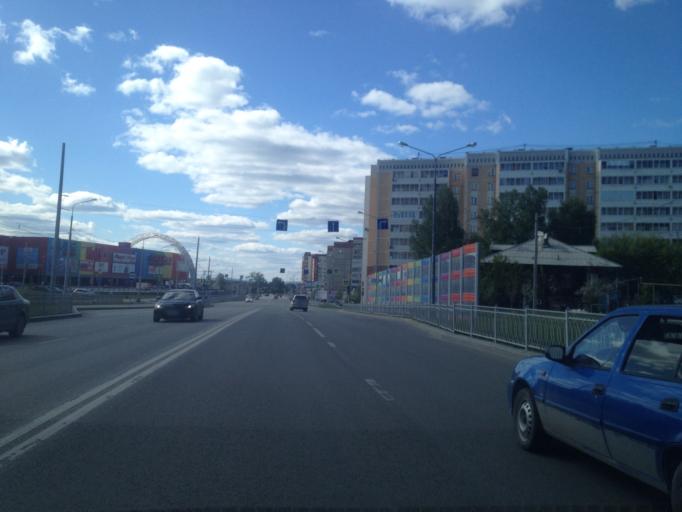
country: RU
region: Sverdlovsk
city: Sovkhoznyy
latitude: 56.8163
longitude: 60.5442
